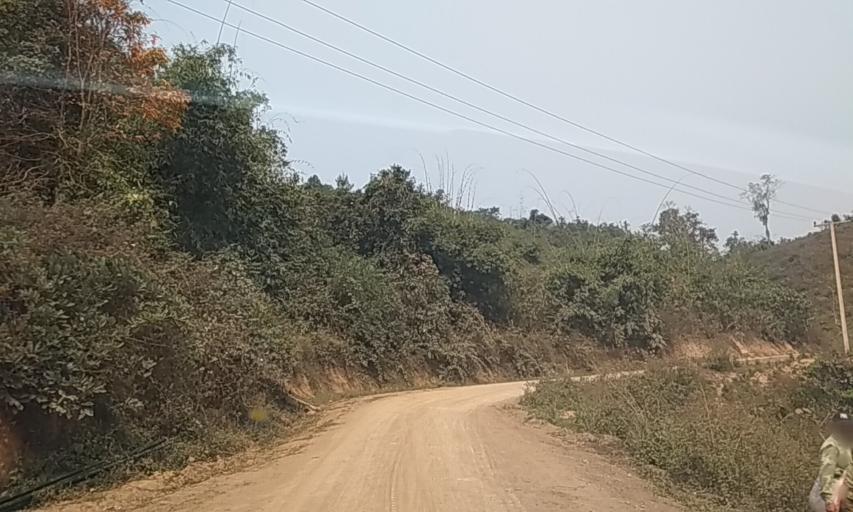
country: VN
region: Huyen Dien Bien
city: Dien Bien Phu
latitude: 21.4202
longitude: 102.7588
